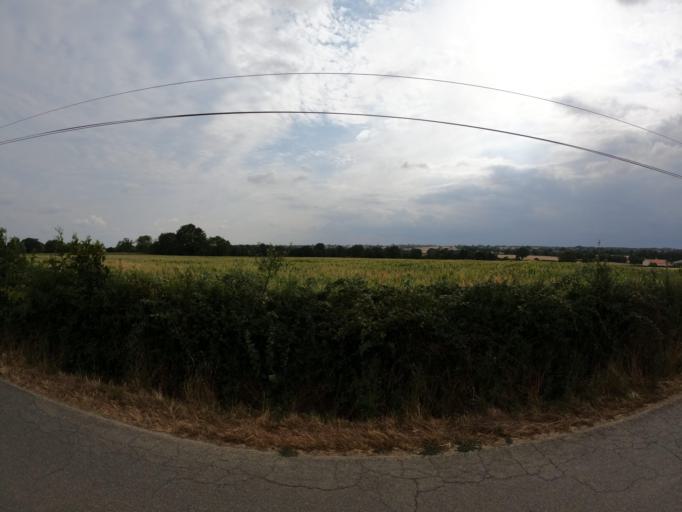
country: FR
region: Pays de la Loire
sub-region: Departement de Maine-et-Loire
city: Saint-Christophe-du-Bois
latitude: 47.0359
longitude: -0.9640
